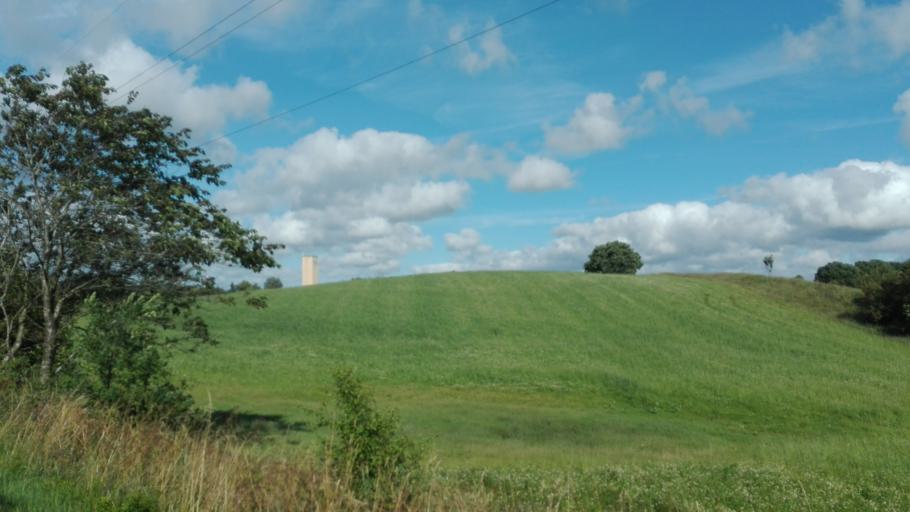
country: DK
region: Central Jutland
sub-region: Silkeborg Kommune
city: Virklund
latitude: 56.0946
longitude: 9.5347
